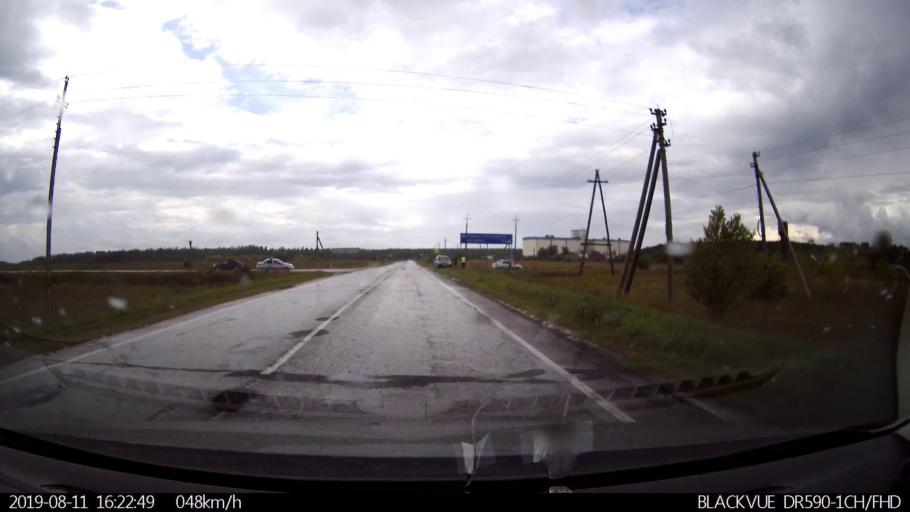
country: RU
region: Ulyanovsk
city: Mayna
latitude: 54.0910
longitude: 47.5911
